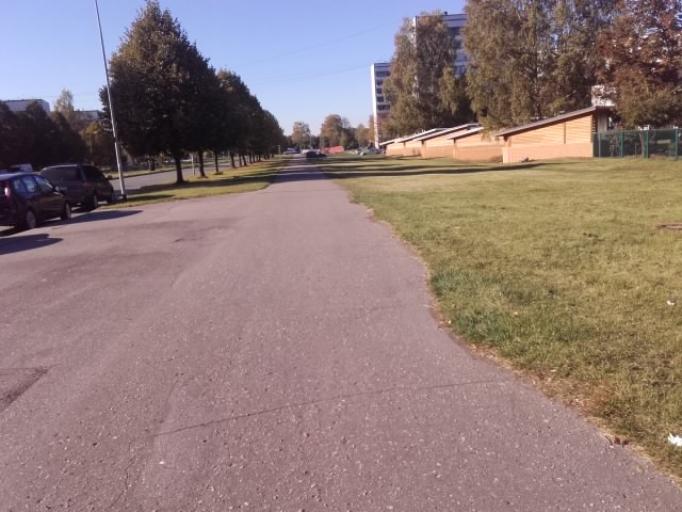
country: LV
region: Stopini
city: Ulbroka
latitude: 56.9404
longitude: 24.2001
